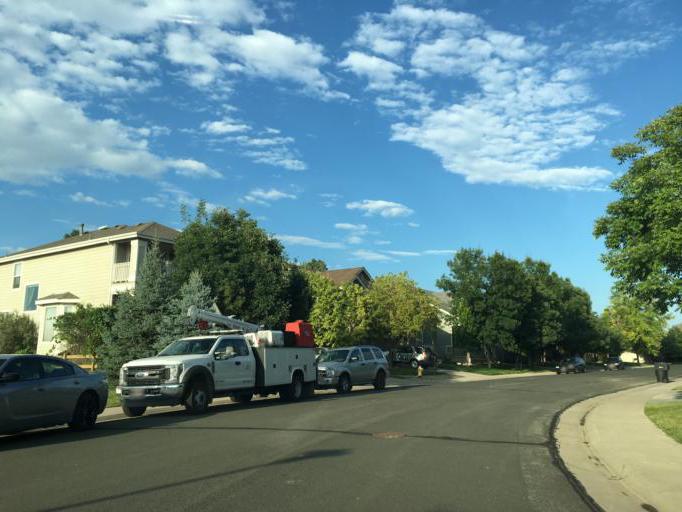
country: US
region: Colorado
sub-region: Adams County
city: Northglenn
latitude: 39.9489
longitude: -104.9547
